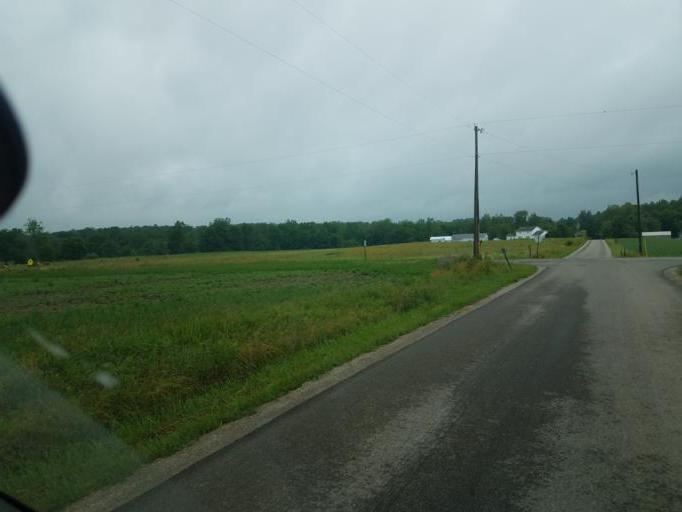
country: US
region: Ohio
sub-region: Richland County
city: Lexington
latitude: 40.6008
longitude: -82.6429
